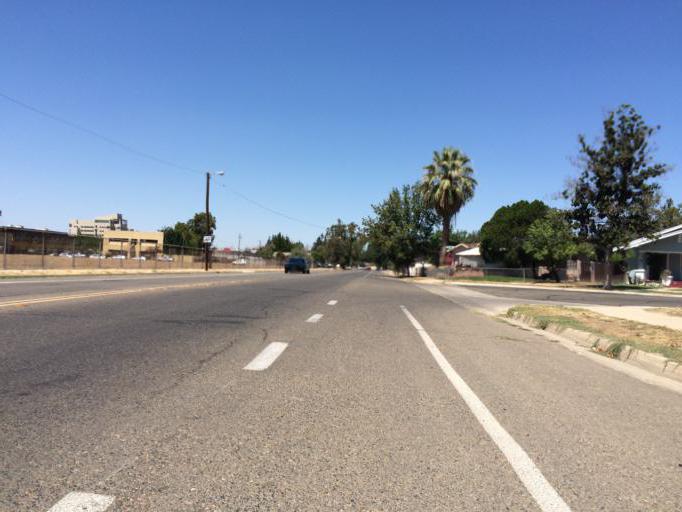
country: US
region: California
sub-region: Fresno County
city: Fresno
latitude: 36.7335
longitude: -119.7730
